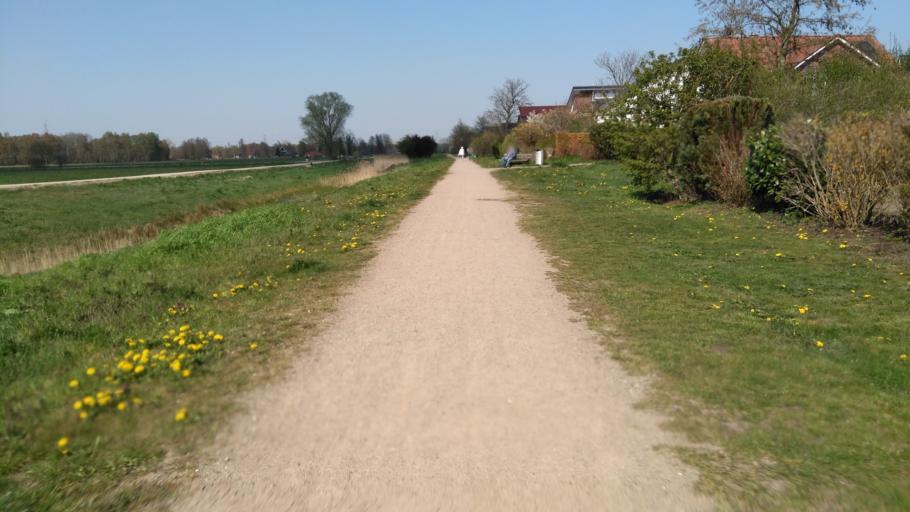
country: DE
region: Lower Saxony
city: Buxtehude
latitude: 53.4773
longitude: 9.6817
